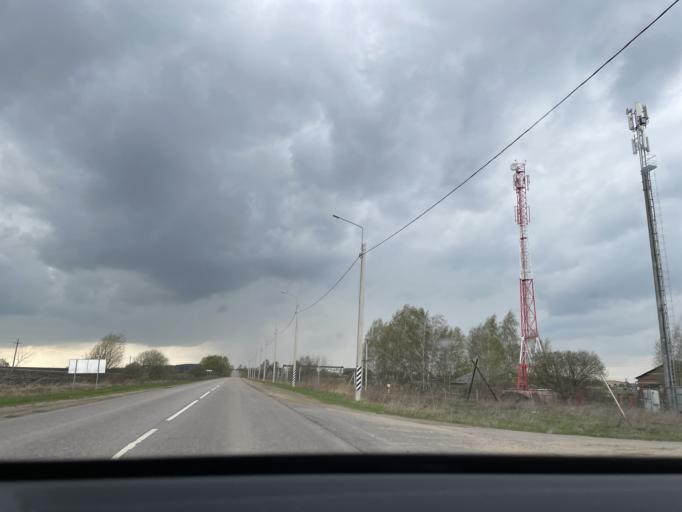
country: RU
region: Tula
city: Novogurovskiy
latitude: 54.5260
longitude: 37.4108
